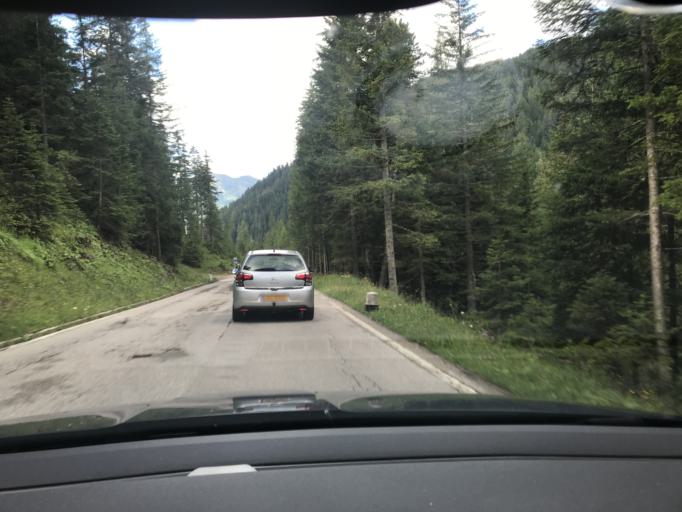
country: IT
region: Veneto
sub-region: Provincia di Belluno
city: Livinallongo del Col di Lana
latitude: 46.5019
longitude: 11.9918
